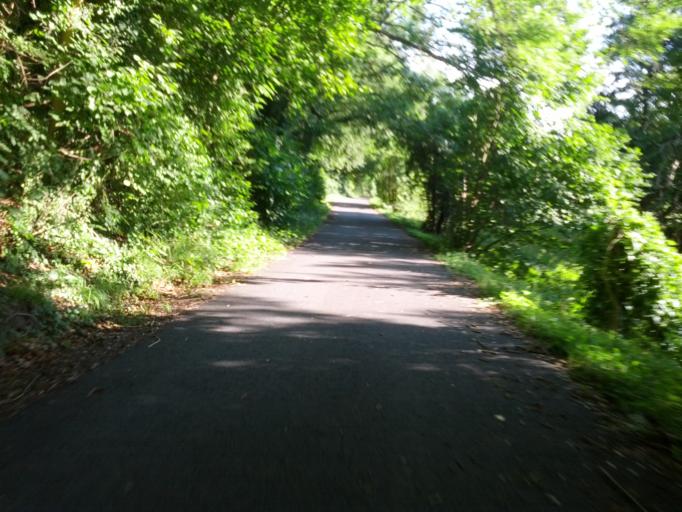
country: DE
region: Thuringia
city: Creuzburg
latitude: 51.0527
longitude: 10.2530
